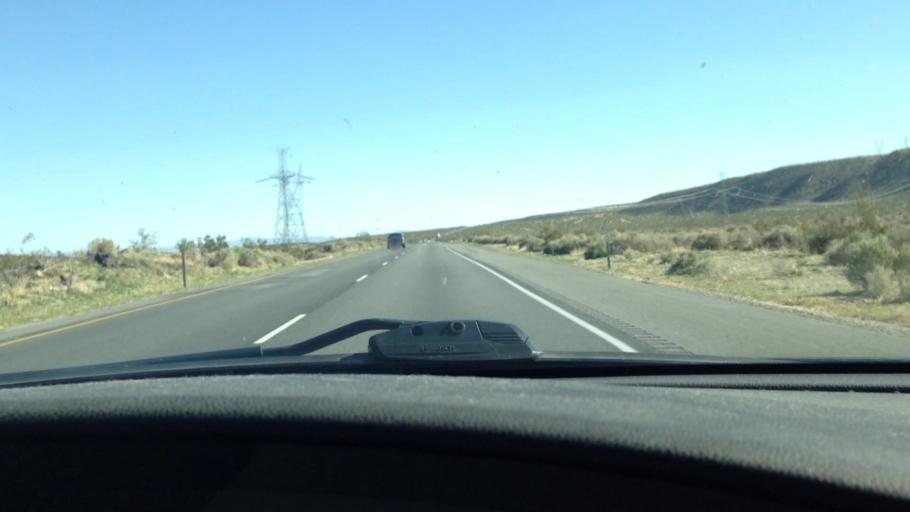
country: US
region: California
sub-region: Kern County
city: Inyokern
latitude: 35.8904
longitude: -117.8961
